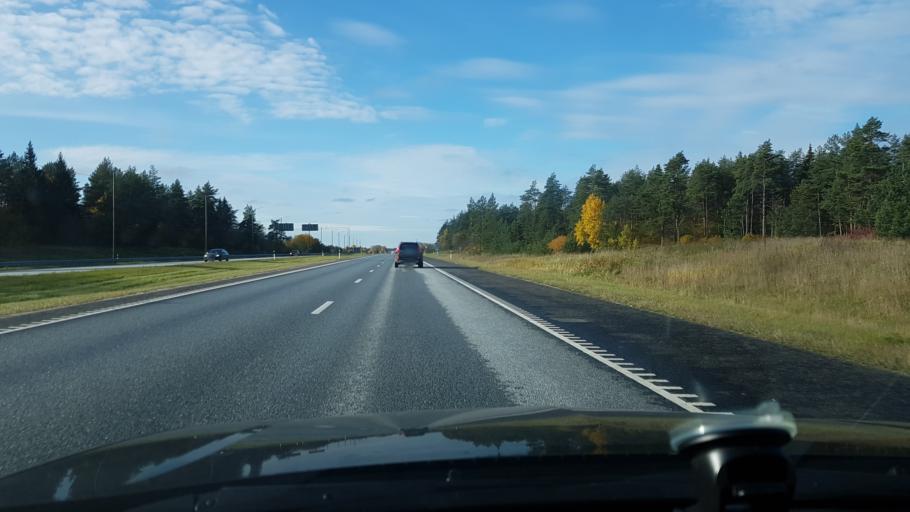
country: EE
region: Harju
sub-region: Kuusalu vald
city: Kuusalu
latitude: 59.4478
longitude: 25.4196
